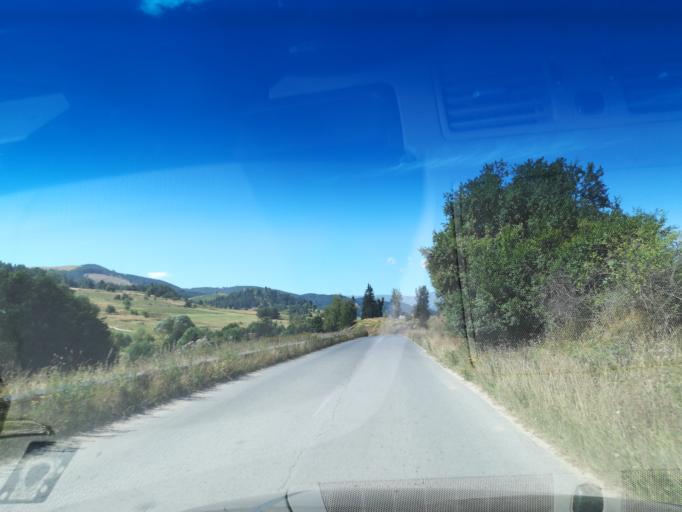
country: BG
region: Sofiya
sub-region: Obshtina Koprivshtitsa
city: Koprivshtitsa
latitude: 42.6115
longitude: 24.3752
